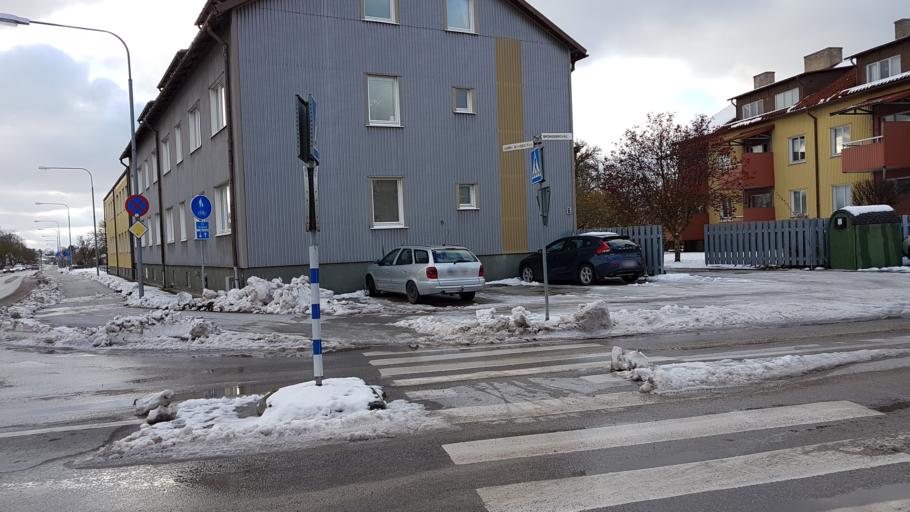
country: SE
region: Gotland
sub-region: Gotland
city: Visby
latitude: 57.6414
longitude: 18.3088
